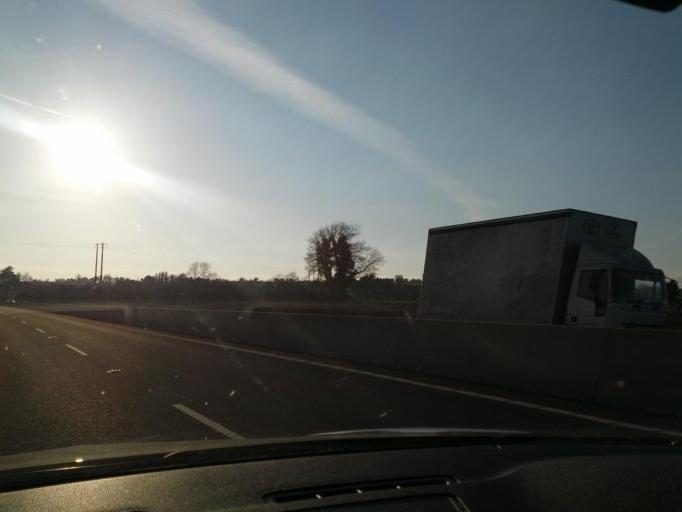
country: IE
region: Munster
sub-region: North Tipperary
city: Roscrea
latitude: 52.9252
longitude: -7.7832
